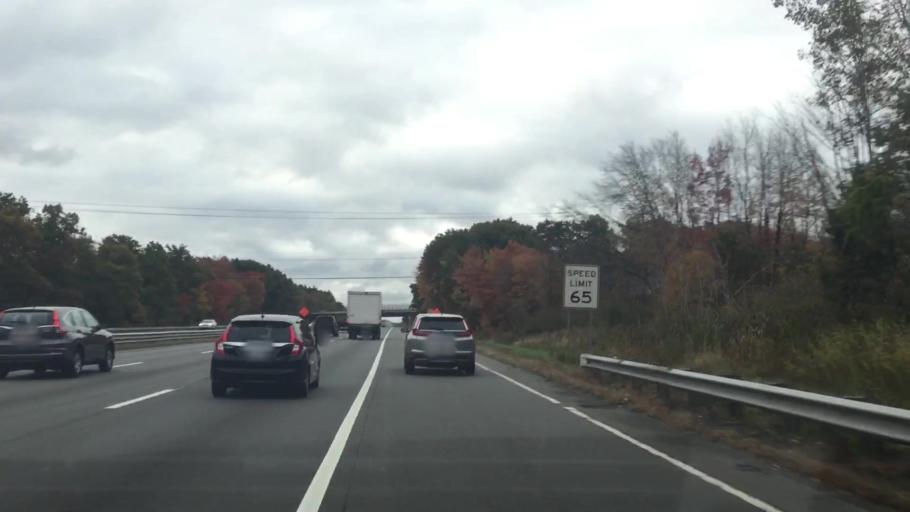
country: US
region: Massachusetts
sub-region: Essex County
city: Methuen
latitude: 42.6848
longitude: -71.2039
